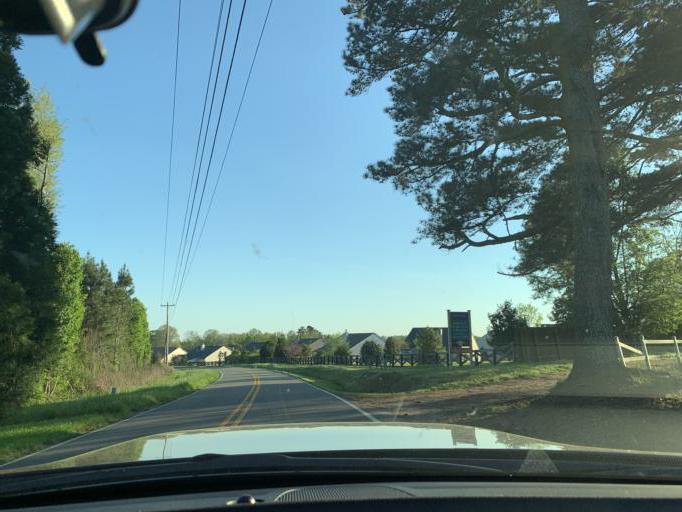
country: US
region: Georgia
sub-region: Forsyth County
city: Cumming
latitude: 34.2352
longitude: -84.2146
